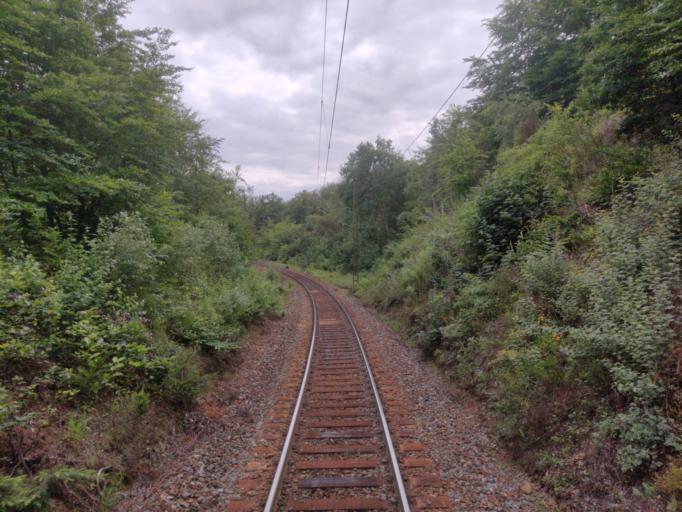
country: DE
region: Saxony-Anhalt
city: Huttenrode
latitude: 51.7893
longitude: 10.9244
